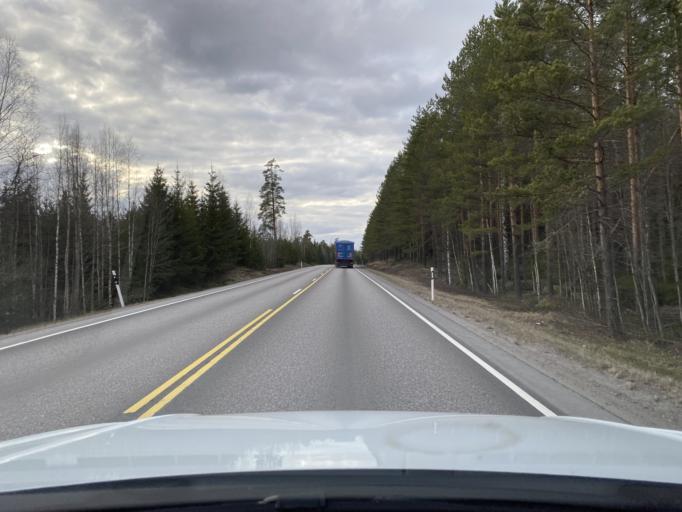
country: FI
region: Uusimaa
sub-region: Helsinki
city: Kaerkoelae
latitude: 60.8211
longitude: 24.0329
